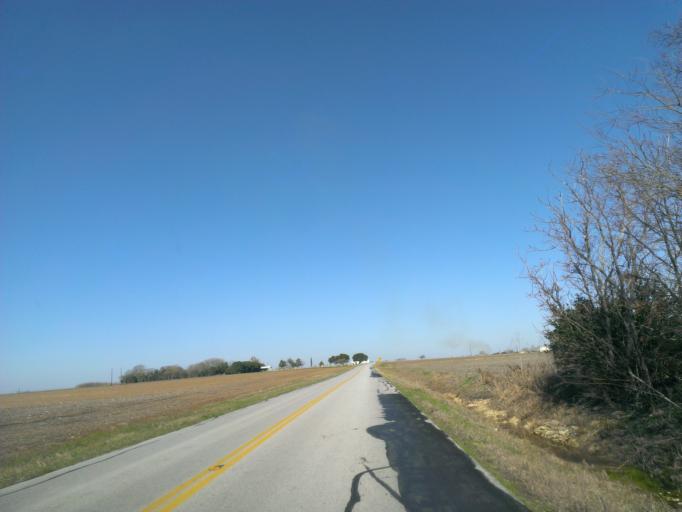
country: US
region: Texas
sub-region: Williamson County
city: Georgetown
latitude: 30.6585
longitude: -97.5810
